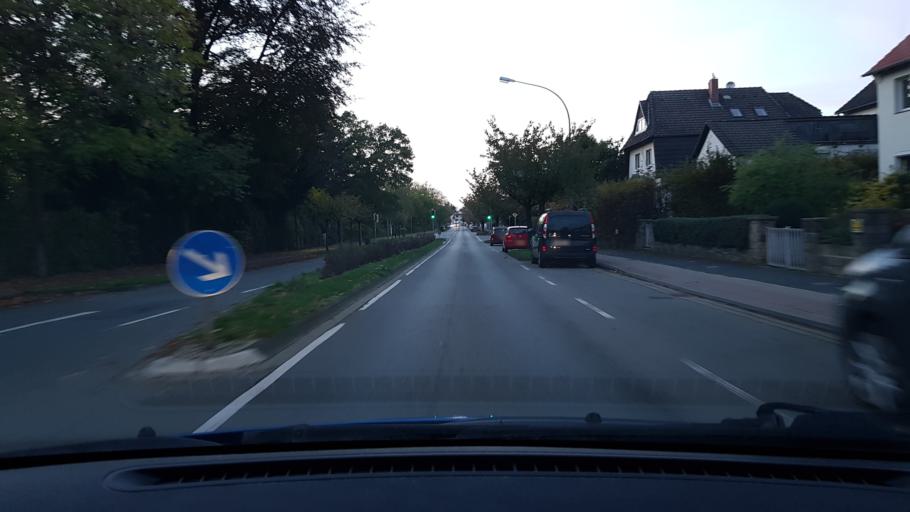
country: DE
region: Lower Saxony
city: Helmstedt
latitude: 52.2296
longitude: 11.0155
